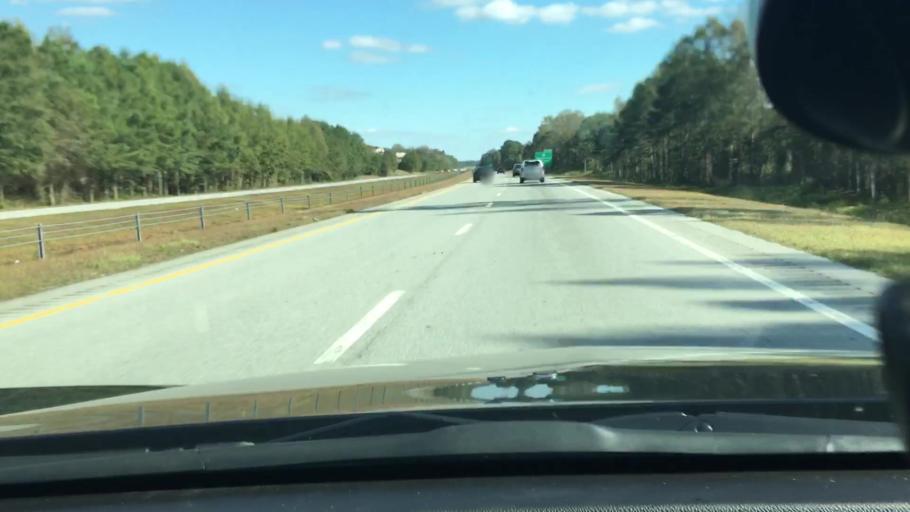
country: US
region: North Carolina
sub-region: Pitt County
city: Farmville
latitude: 35.6213
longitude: -77.7023
